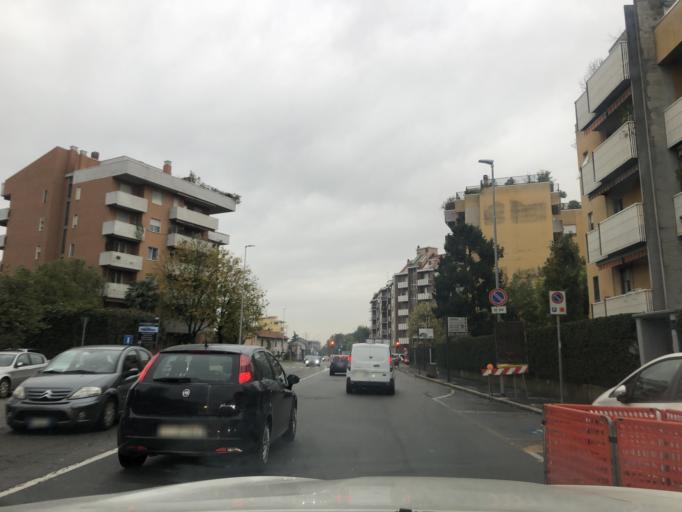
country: IT
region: Lombardy
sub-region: Citta metropolitana di Milano
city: Cesano Boscone
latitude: 45.4472
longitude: 9.0985
